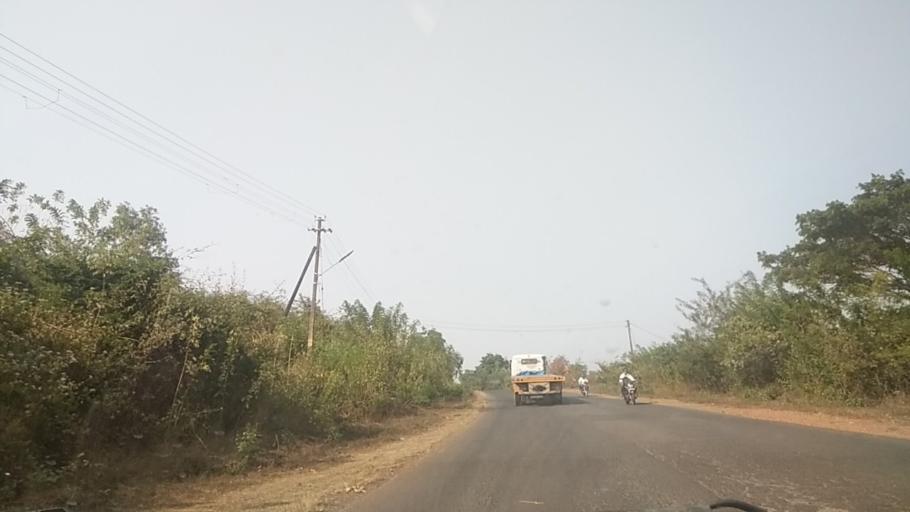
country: IN
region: Goa
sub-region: North Goa
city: Colovale
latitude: 15.6758
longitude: 73.8371
